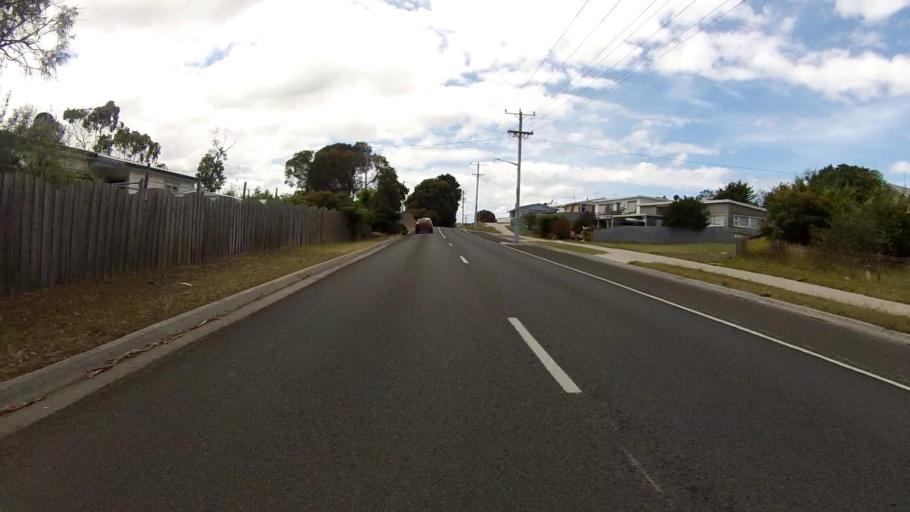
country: AU
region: Tasmania
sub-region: Sorell
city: Sorell
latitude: -42.8560
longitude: 147.6185
